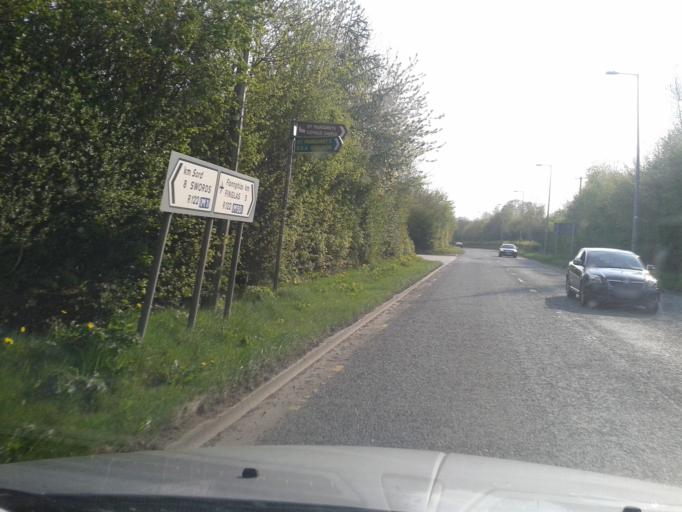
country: IE
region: Leinster
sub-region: Dublin City
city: Finglas
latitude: 53.4293
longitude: -6.3006
